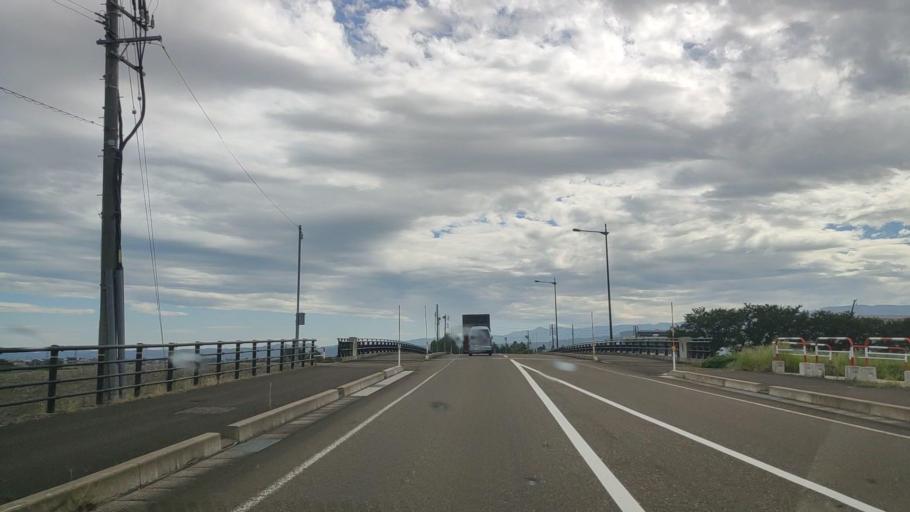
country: JP
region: Niigata
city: Joetsu
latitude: 37.0825
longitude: 138.2552
